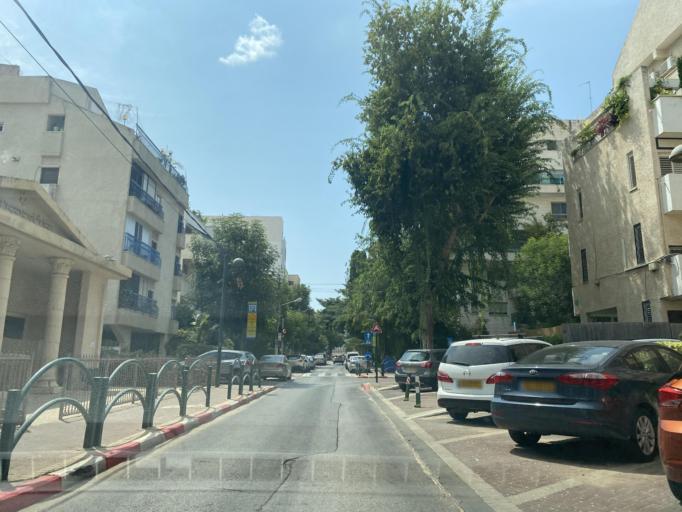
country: IL
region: Central District
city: Kfar Saba
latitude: 32.1720
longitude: 34.9044
